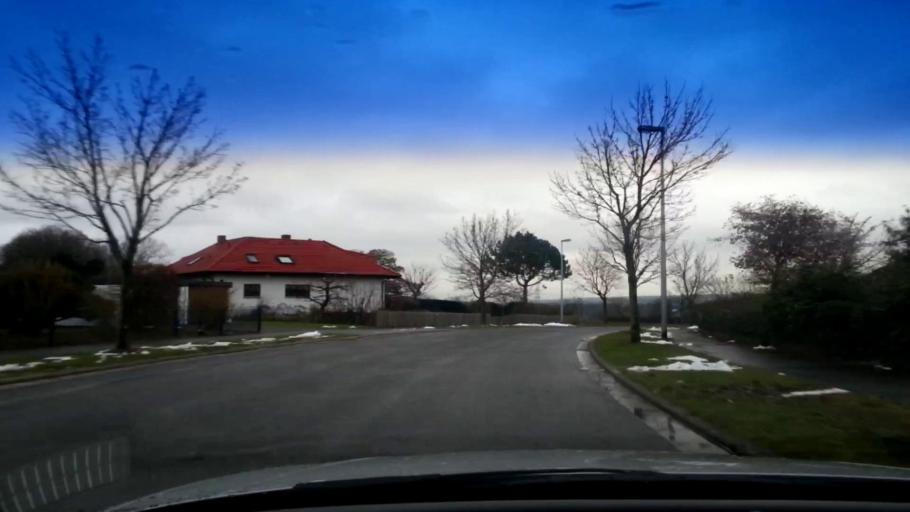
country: DE
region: Bavaria
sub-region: Upper Franconia
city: Gundelsheim
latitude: 49.9415
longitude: 10.9256
